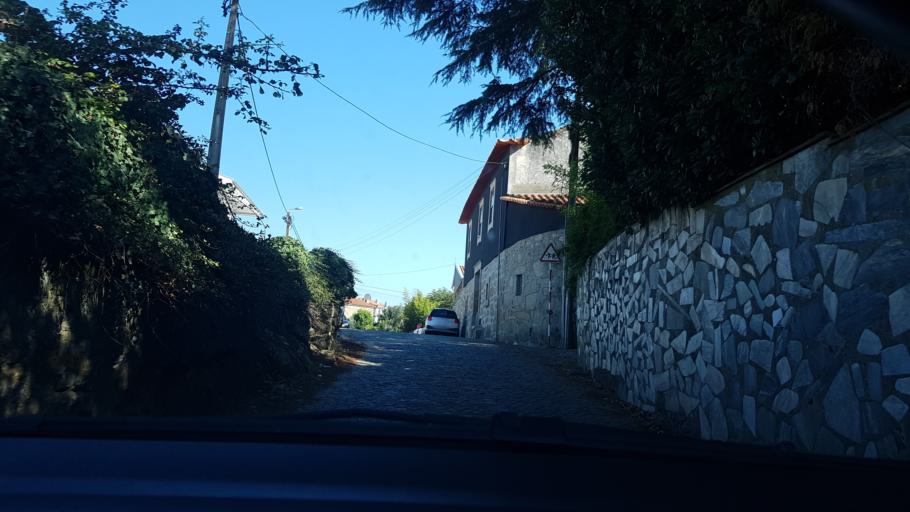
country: PT
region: Porto
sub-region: Gondomar
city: Baguim do Monte
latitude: 41.1918
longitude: -8.5428
